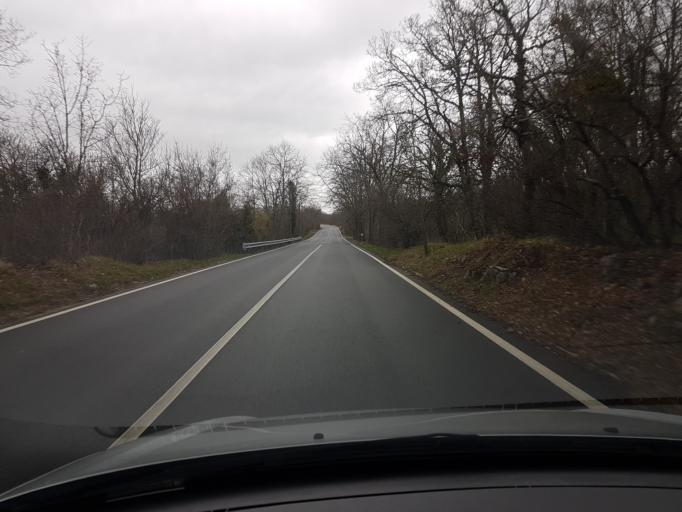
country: IT
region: Friuli Venezia Giulia
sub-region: Provincia di Trieste
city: Sgonico
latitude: 45.7345
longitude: 13.7267
